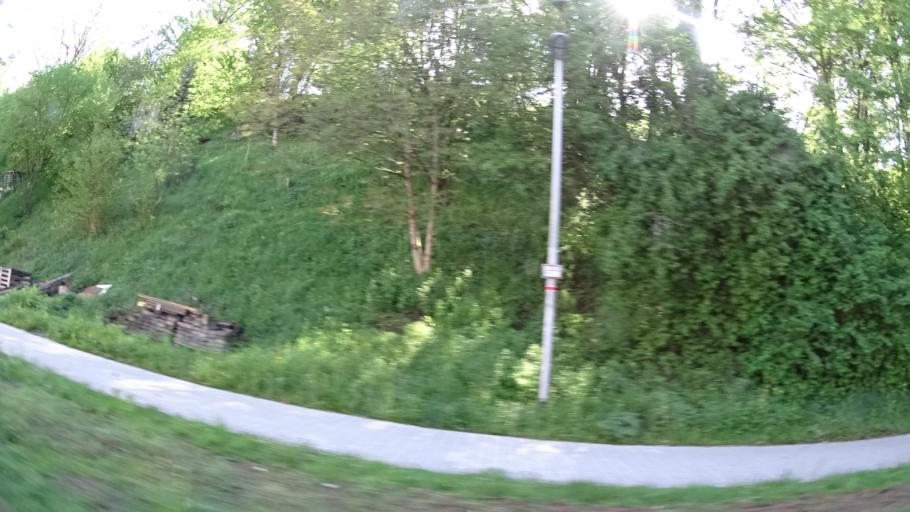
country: DE
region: Baden-Wuerttemberg
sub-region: Karlsruhe Region
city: Ebhausen
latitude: 48.5834
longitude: 8.6762
